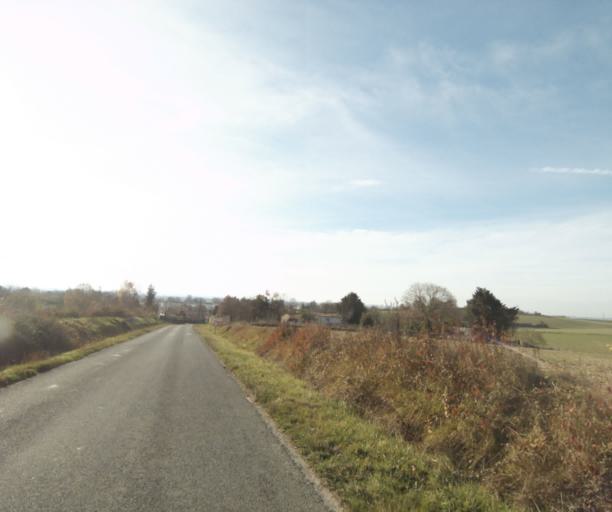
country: FR
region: Poitou-Charentes
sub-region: Departement de la Charente-Maritime
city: Chaniers
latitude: 45.7244
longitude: -0.5542
